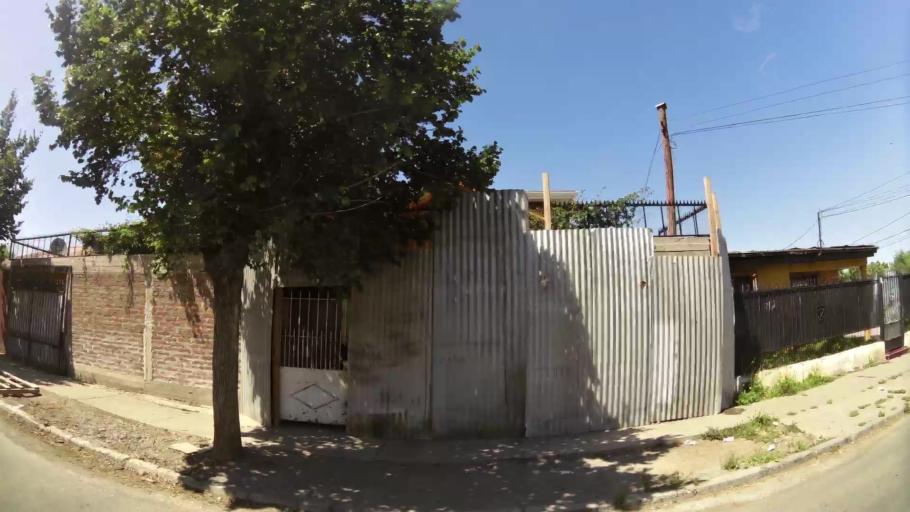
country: CL
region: Santiago Metropolitan
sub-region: Provincia de Santiago
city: La Pintana
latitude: -33.5641
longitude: -70.6586
